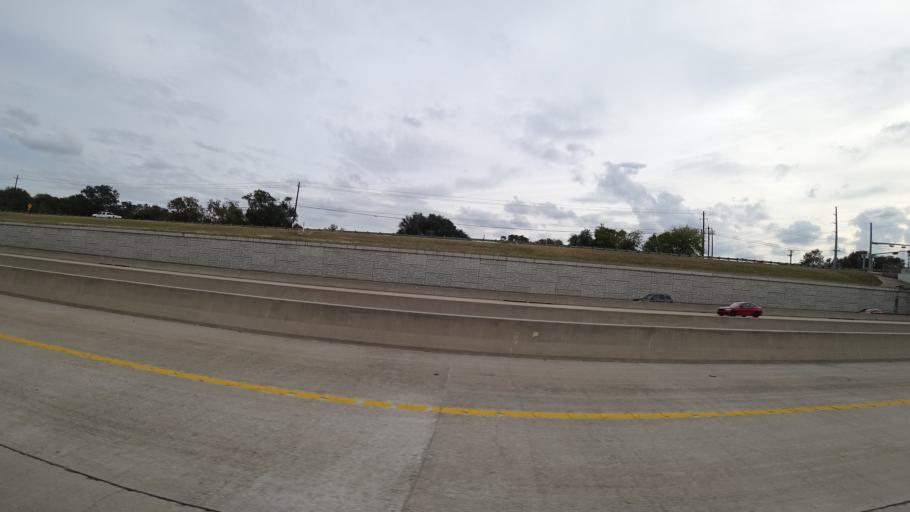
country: US
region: Texas
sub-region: Williamson County
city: Jollyville
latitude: 30.4769
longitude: -97.7637
